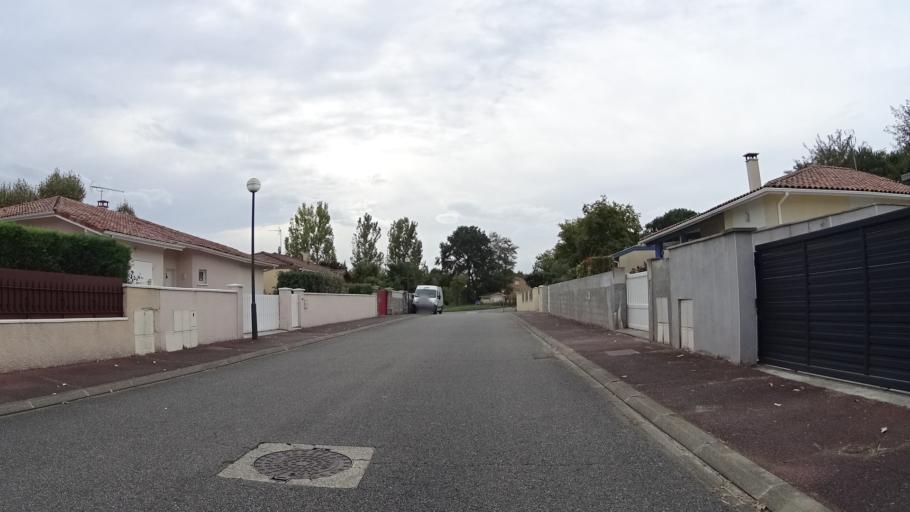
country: FR
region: Aquitaine
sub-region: Departement des Landes
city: Saint-Paul-les-Dax
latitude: 43.7304
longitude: -1.0804
